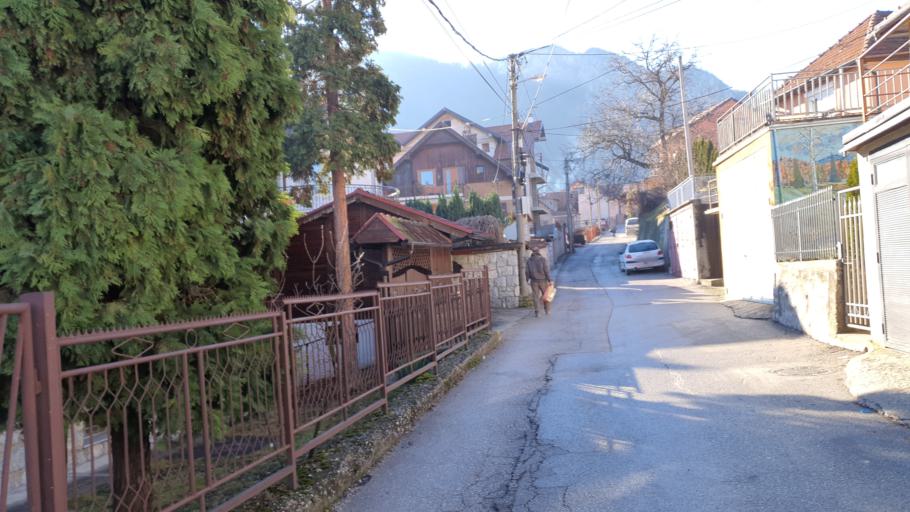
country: RS
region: Central Serbia
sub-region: Zlatiborski Okrug
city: Uzice
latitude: 43.8551
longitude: 19.8326
